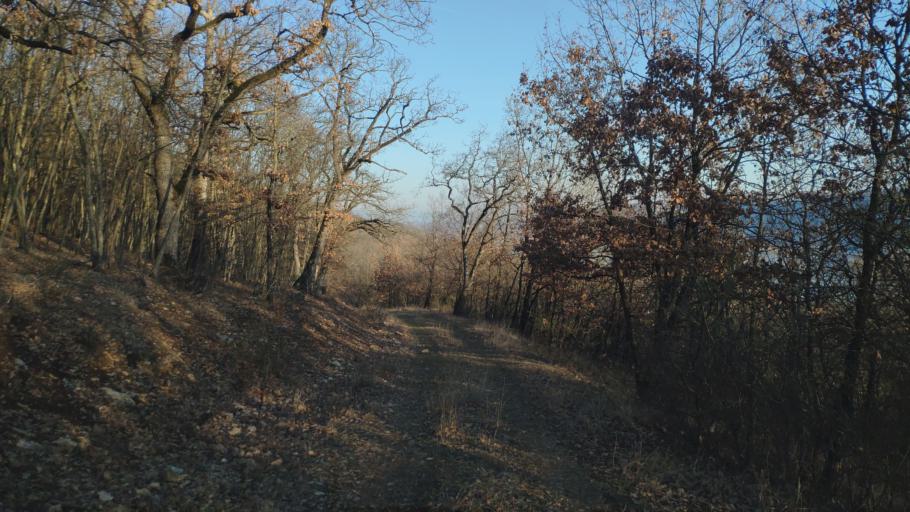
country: SK
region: Kosicky
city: Roznava
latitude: 48.6051
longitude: 20.7231
